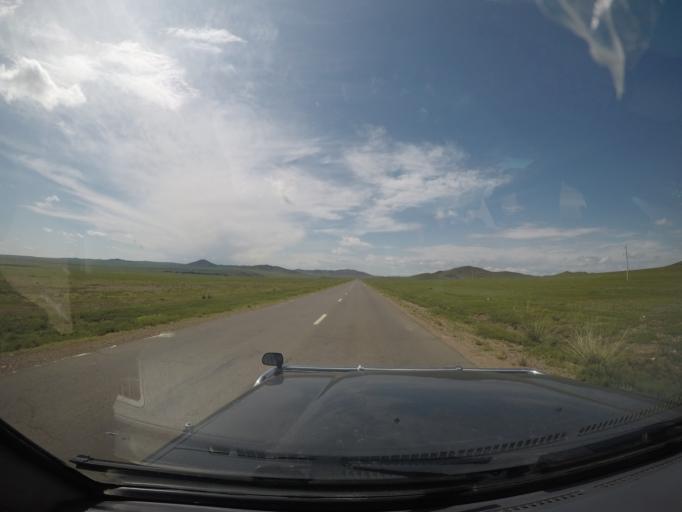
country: MN
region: Hentiy
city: Moron
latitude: 47.3799
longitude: 110.3789
